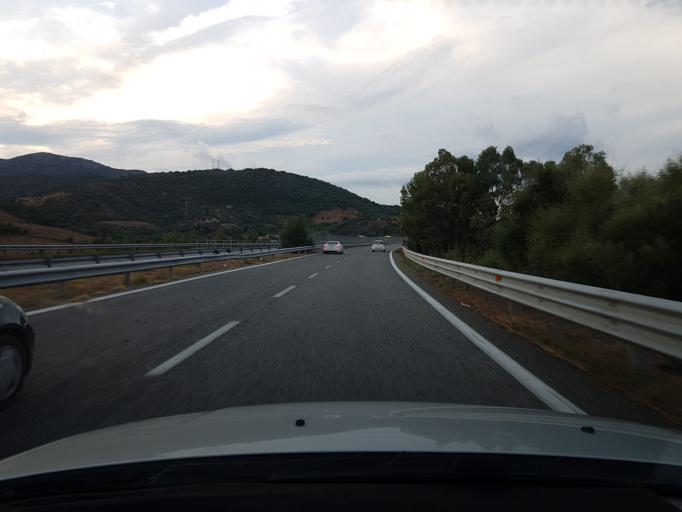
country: IT
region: Sardinia
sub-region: Provincia di Olbia-Tempio
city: San Teodoro
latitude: 40.7289
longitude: 9.6517
